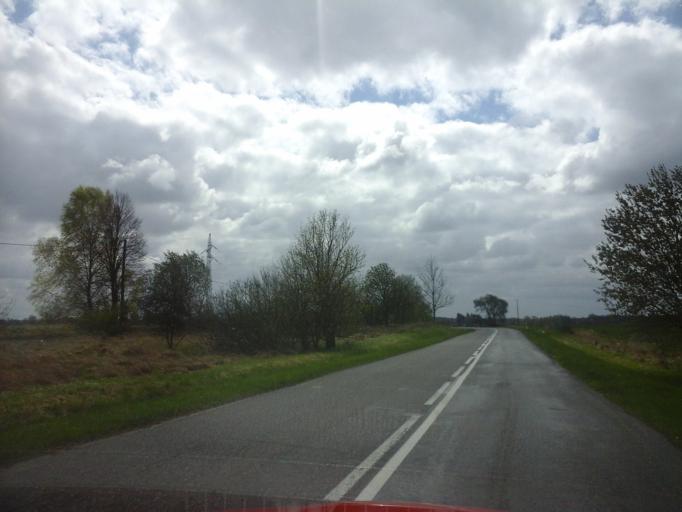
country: PL
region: West Pomeranian Voivodeship
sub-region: Powiat choszczenski
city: Bierzwnik
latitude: 53.0592
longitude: 15.6631
